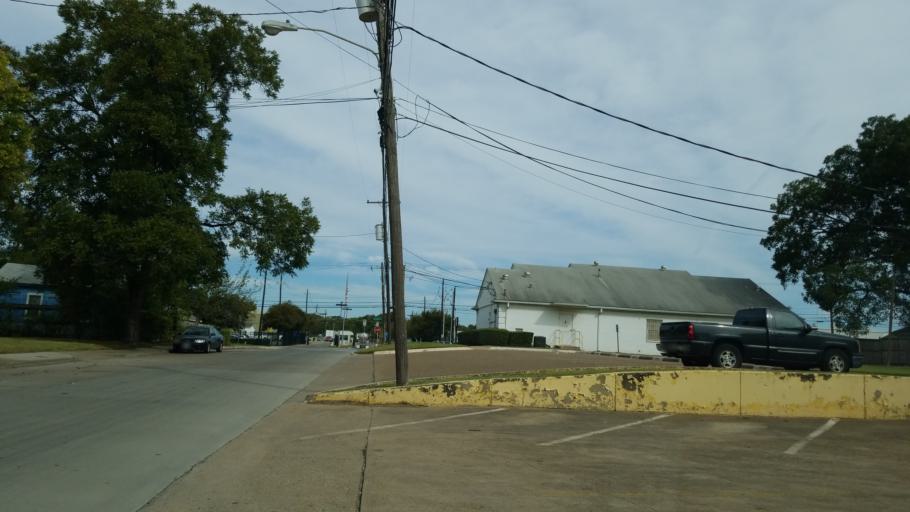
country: US
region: Texas
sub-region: Dallas County
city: Dallas
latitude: 32.7820
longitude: -96.7402
